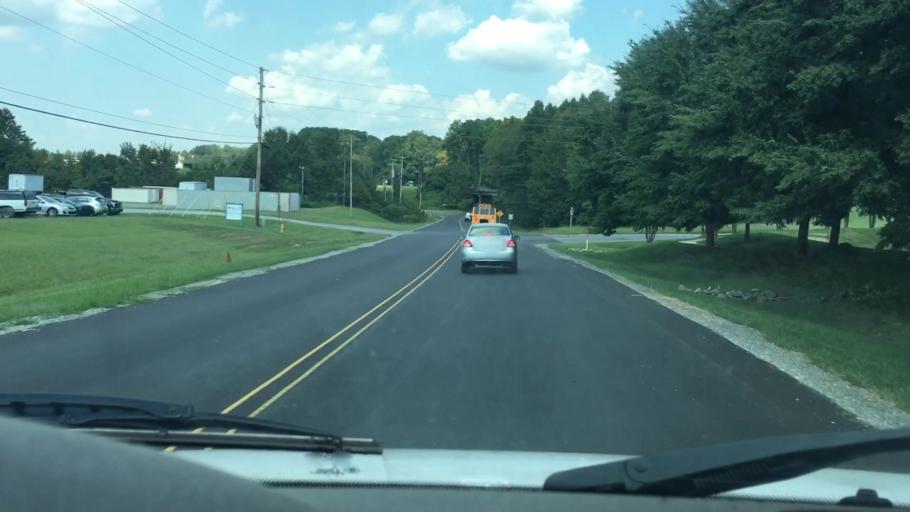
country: US
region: North Carolina
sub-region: Mecklenburg County
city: Huntersville
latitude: 35.3959
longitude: -80.8519
